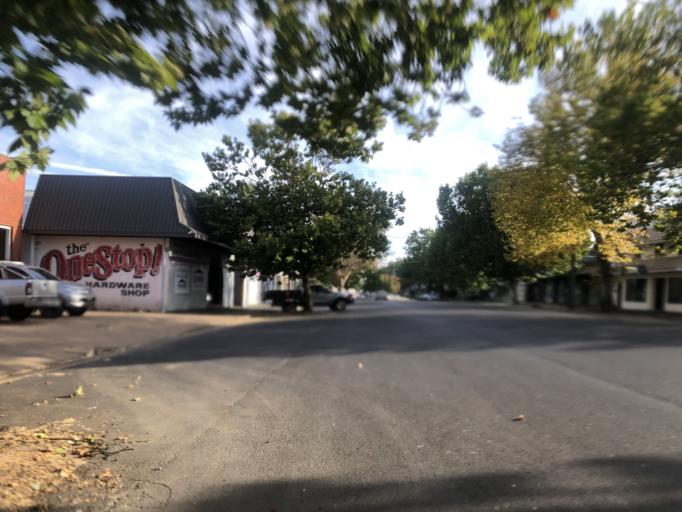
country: AU
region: New South Wales
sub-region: Orange Municipality
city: Orange
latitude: -33.2873
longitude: 149.1004
